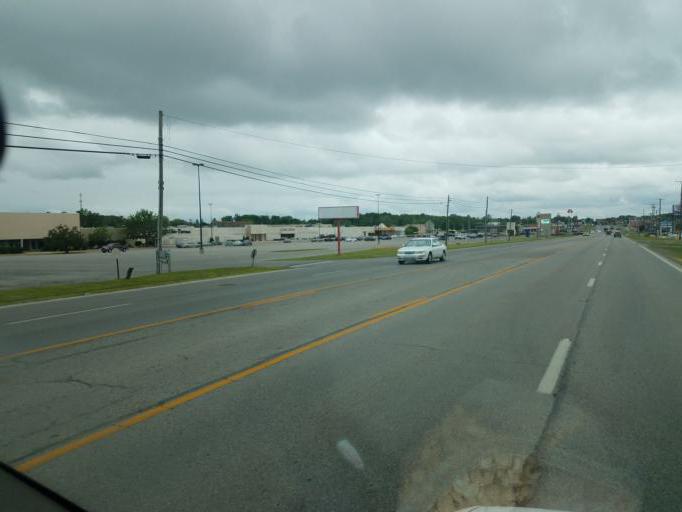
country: US
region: Ohio
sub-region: Marion County
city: Marion
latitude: 40.5598
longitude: -83.1182
